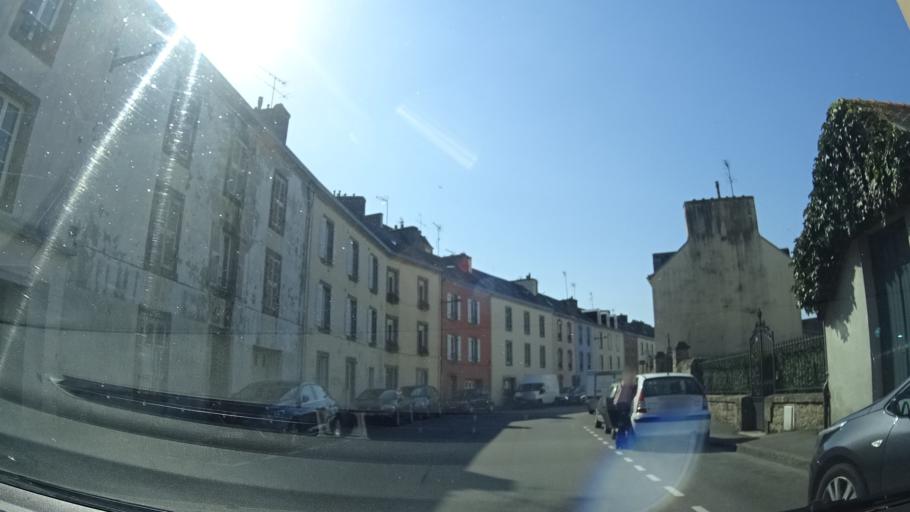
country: FR
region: Brittany
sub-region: Departement du Finistere
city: Douarnenez
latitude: 48.0882
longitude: -4.3292
